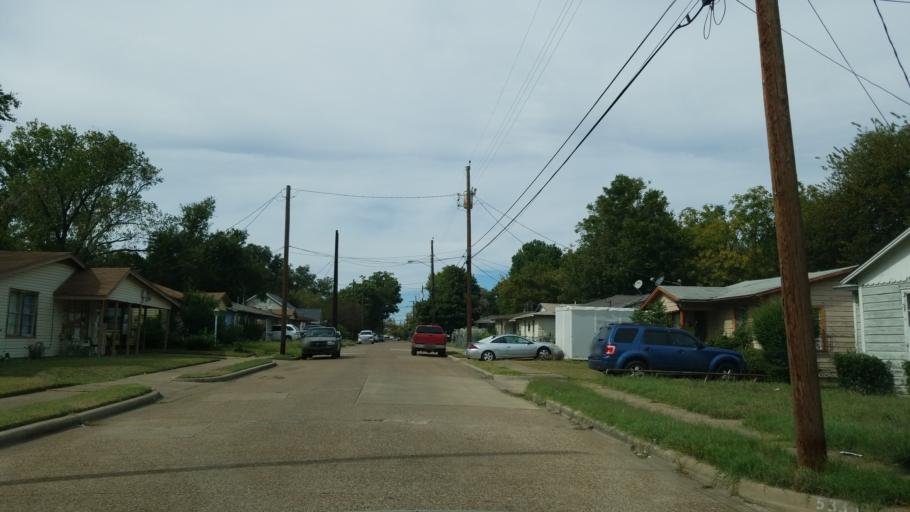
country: US
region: Texas
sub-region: Dallas County
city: Dallas
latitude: 32.7625
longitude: -96.7334
